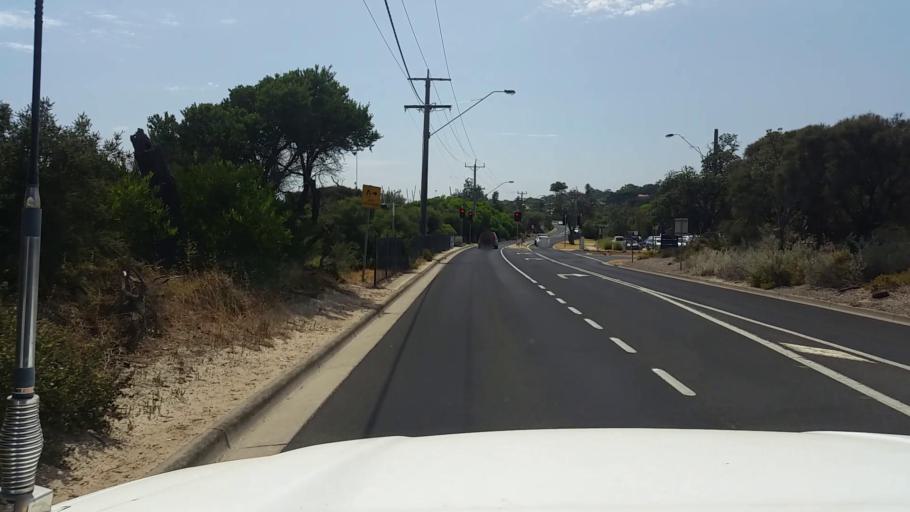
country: AU
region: Victoria
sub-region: Mornington Peninsula
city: Mount Martha
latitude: -38.2671
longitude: 145.0130
